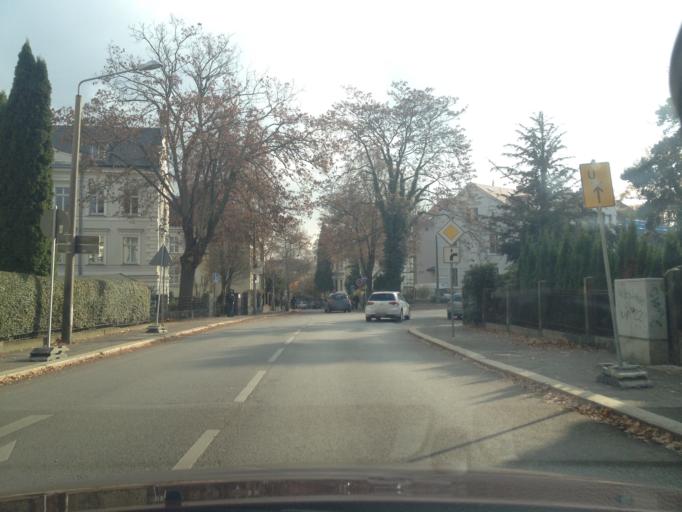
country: DE
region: Saxony
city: Goerlitz
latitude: 51.1505
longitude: 14.9906
